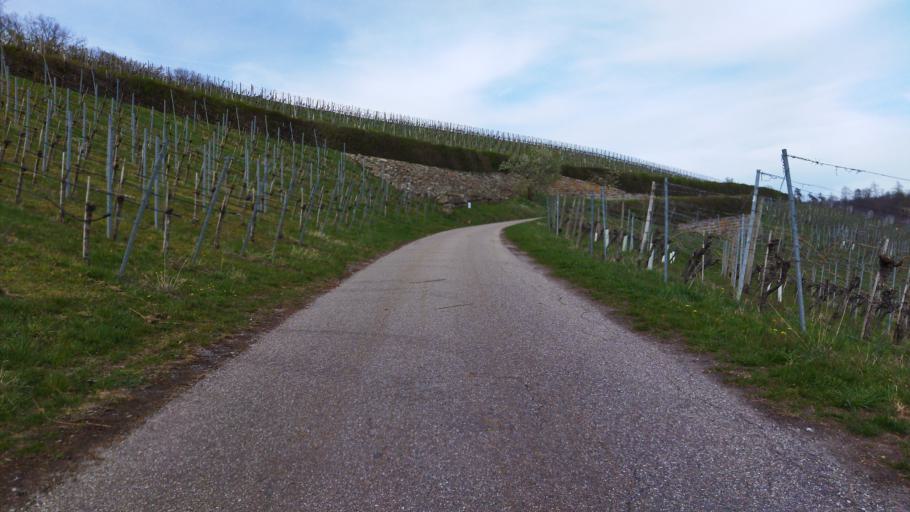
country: DE
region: Baden-Wuerttemberg
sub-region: Regierungsbezirk Stuttgart
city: Beilstein
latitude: 49.0696
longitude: 9.3227
